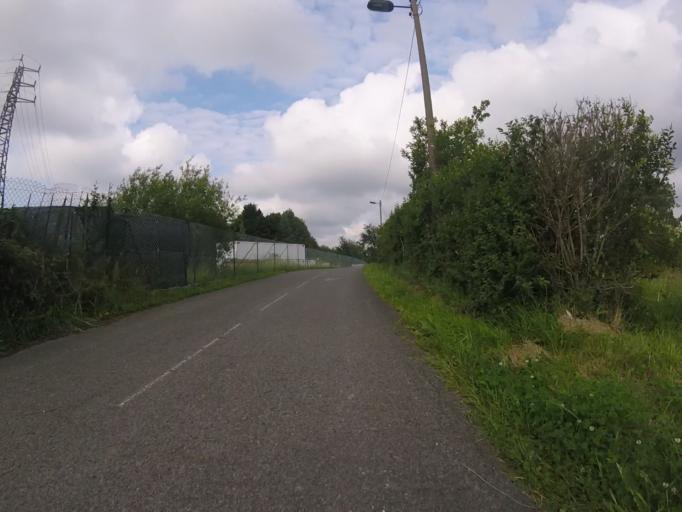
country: ES
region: Basque Country
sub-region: Provincia de Guipuzcoa
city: Astigarraga
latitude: 43.3066
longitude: -1.9440
